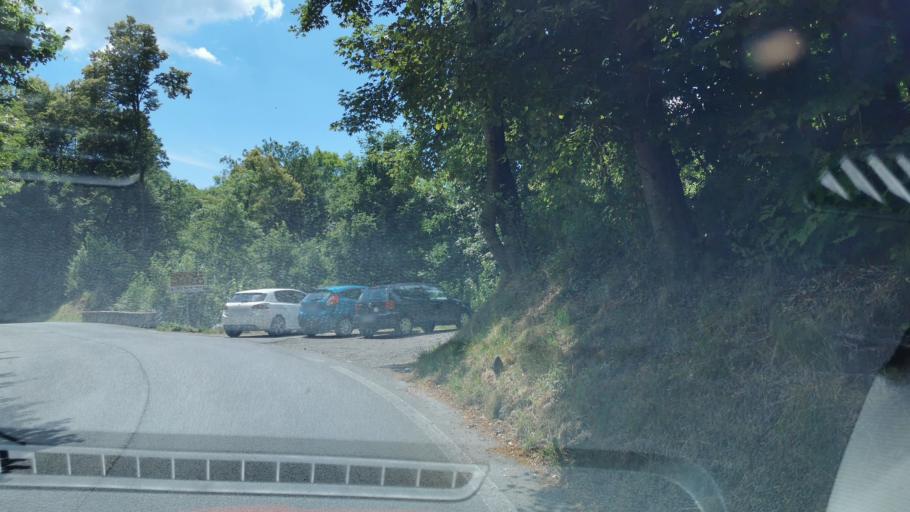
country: IT
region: Lombardy
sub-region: Provincia di Como
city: Pellio Intelvi
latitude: 45.9759
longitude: 9.0508
